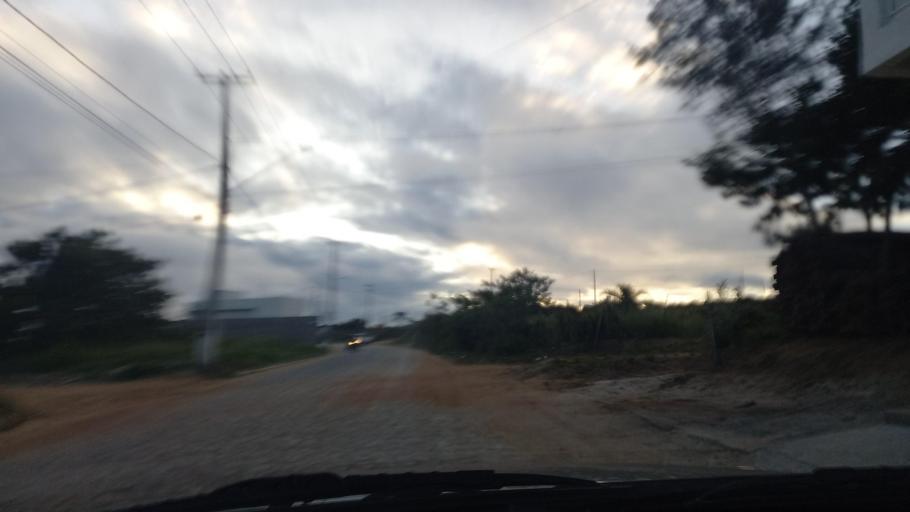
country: BR
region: Pernambuco
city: Garanhuns
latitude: -8.8912
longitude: -36.4458
